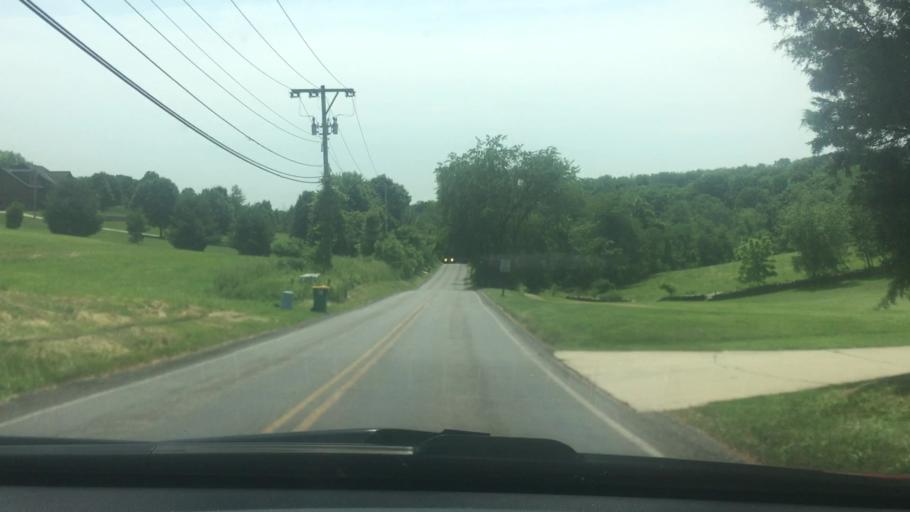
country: US
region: Pennsylvania
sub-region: Allegheny County
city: Bridgeville
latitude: 40.3459
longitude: -80.1499
